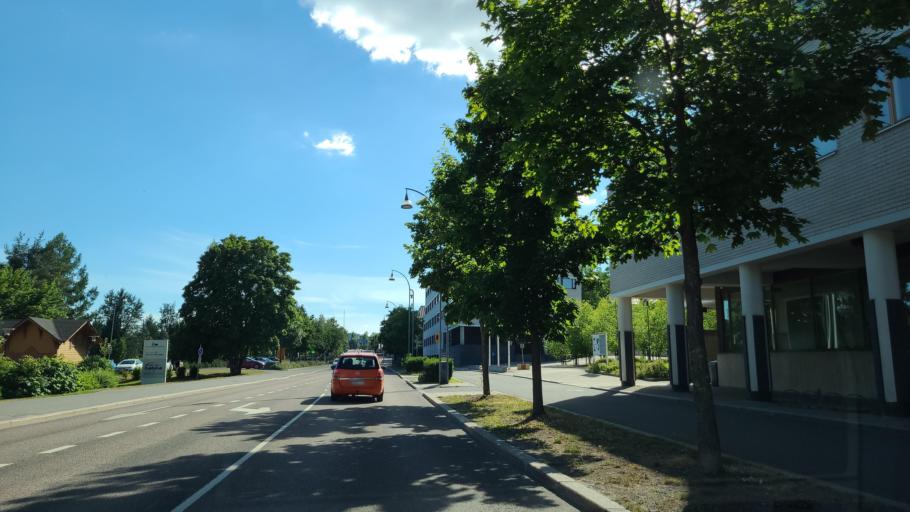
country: FI
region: Central Finland
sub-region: Jyvaeskylae
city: Jyvaeskylae
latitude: 62.2395
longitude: 25.7493
